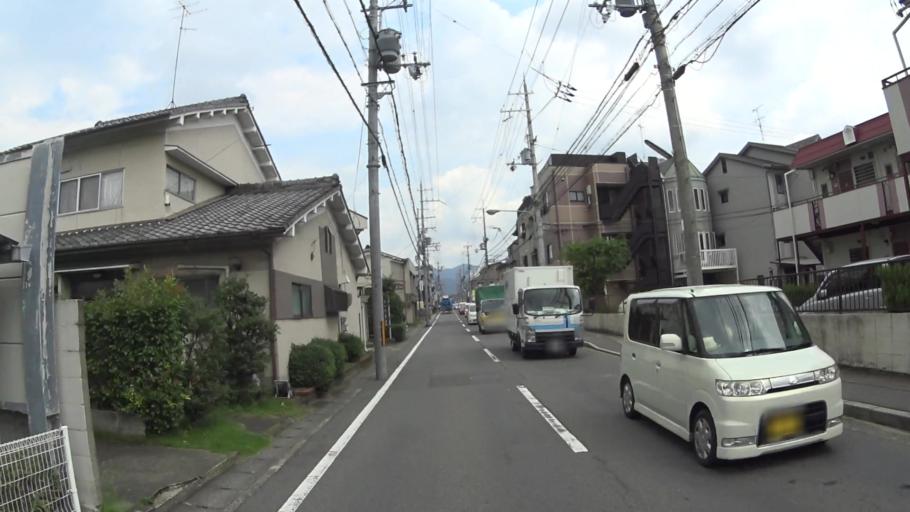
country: JP
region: Kyoto
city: Muko
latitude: 35.0042
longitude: 135.7062
